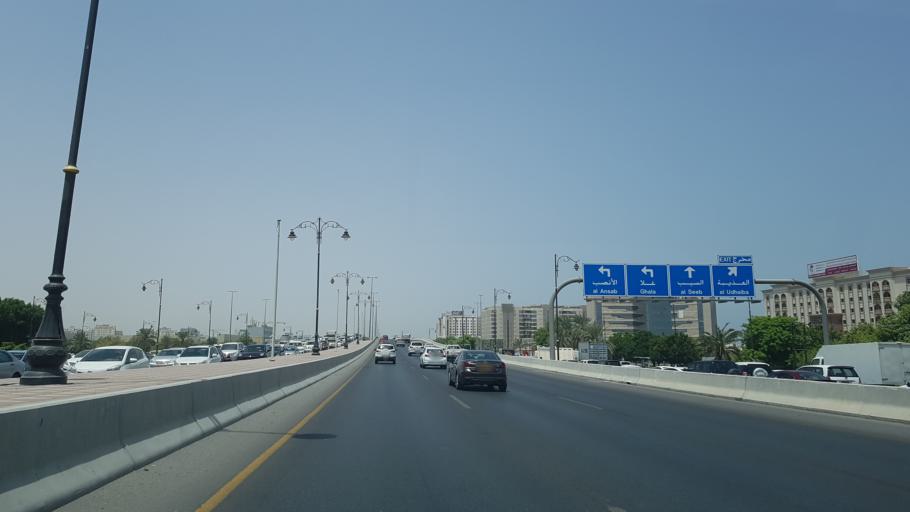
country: OM
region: Muhafazat Masqat
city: Bawshar
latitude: 23.5873
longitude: 58.3856
